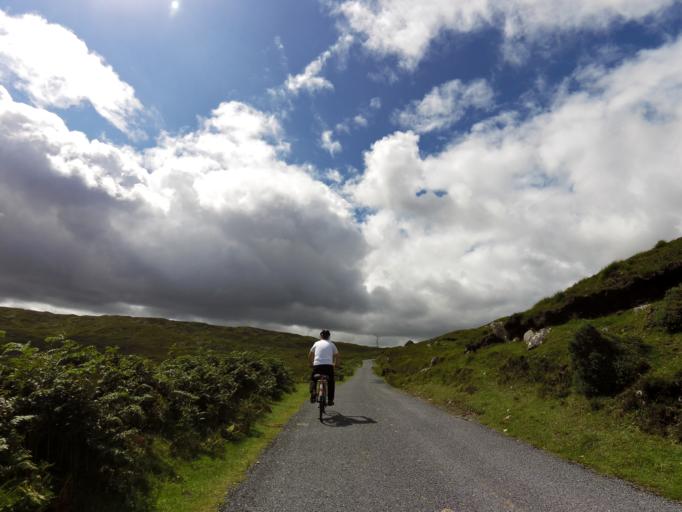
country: IE
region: Connaught
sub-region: County Galway
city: Oughterard
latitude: 53.3905
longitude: -9.3411
